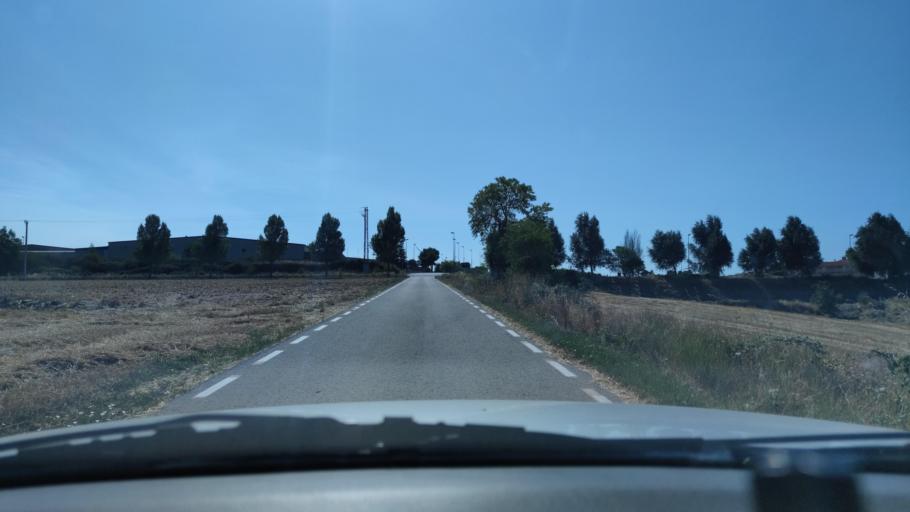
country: ES
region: Catalonia
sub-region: Provincia de Lleida
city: Sant Guim de Freixenet
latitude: 41.6456
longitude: 1.4159
